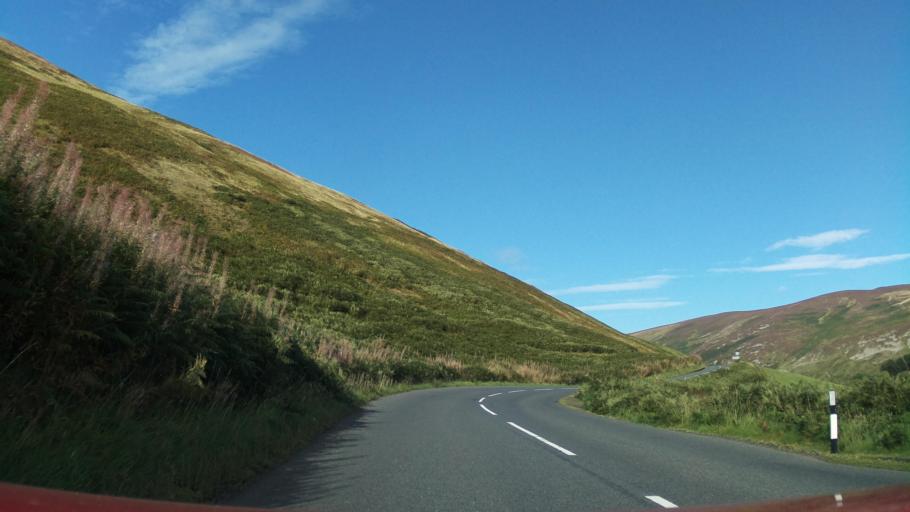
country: GB
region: Scotland
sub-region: South Lanarkshire
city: Biggar
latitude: 55.5570
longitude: -3.4012
